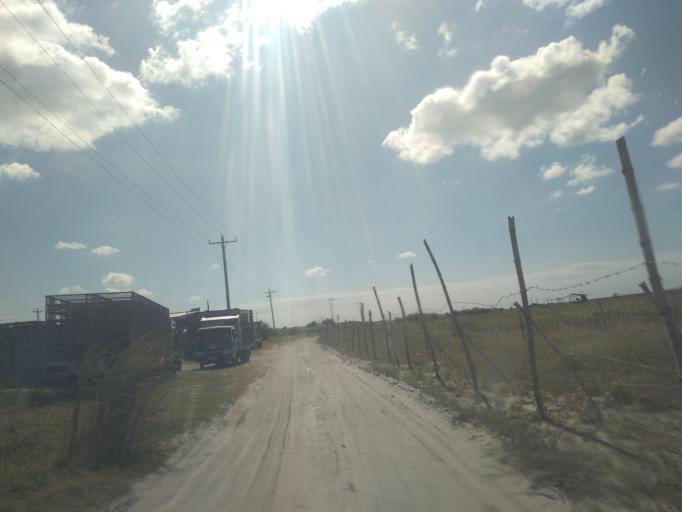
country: PH
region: Central Luzon
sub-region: Province of Pampanga
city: Balas
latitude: 15.0634
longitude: 120.5931
